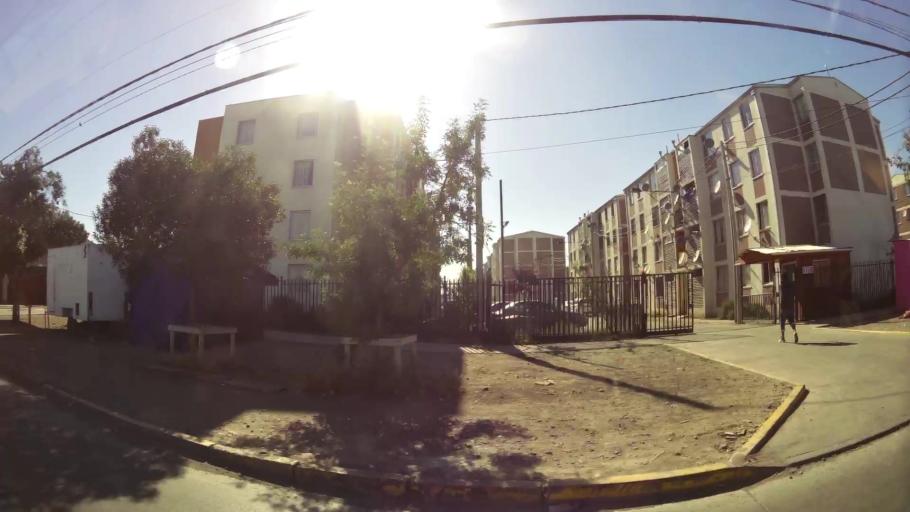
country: CL
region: Santiago Metropolitan
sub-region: Provincia de Maipo
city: San Bernardo
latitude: -33.5548
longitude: -70.6925
